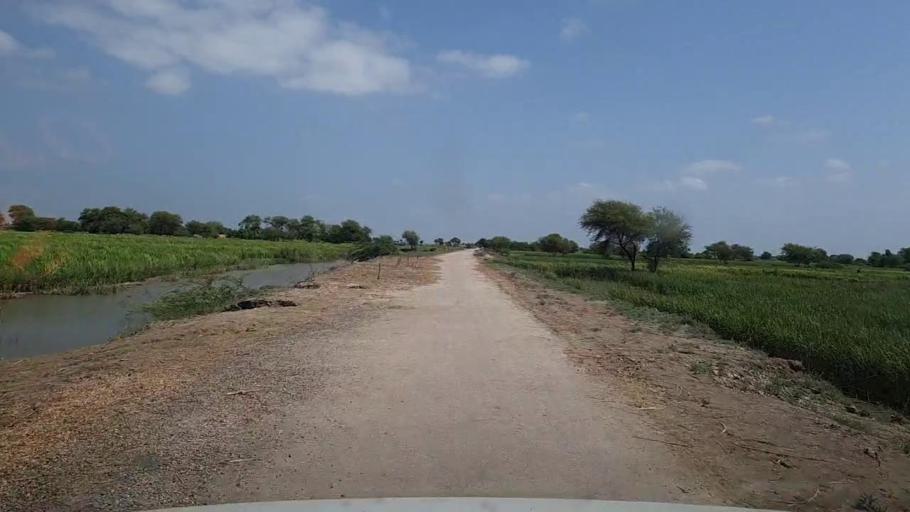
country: PK
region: Sindh
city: Kario
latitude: 24.6842
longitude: 68.5944
